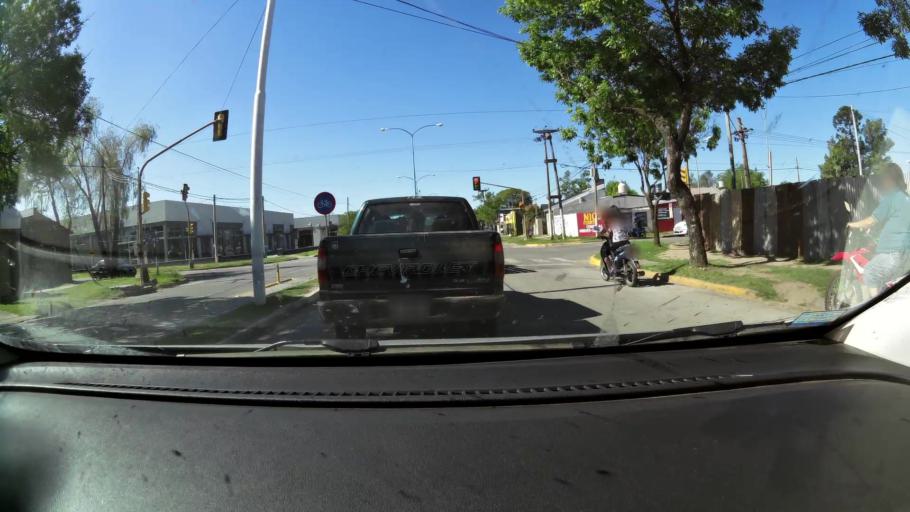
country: AR
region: Santa Fe
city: Rafaela
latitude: -31.2390
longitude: -61.4885
